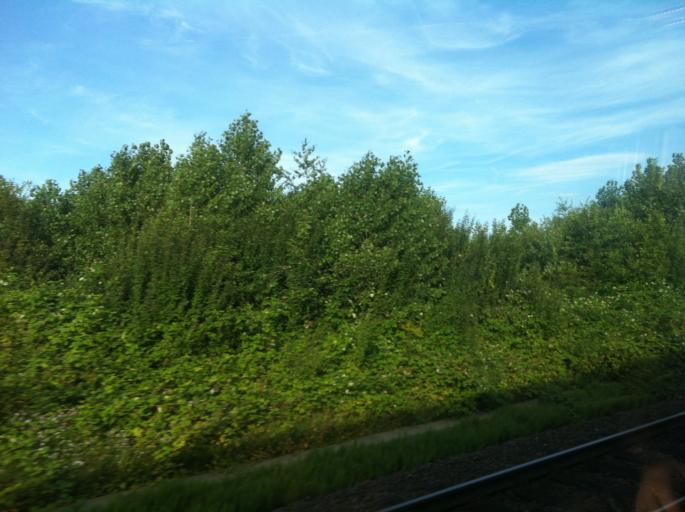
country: DE
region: North Rhine-Westphalia
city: Niederkassel
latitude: 50.7876
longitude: 7.0263
